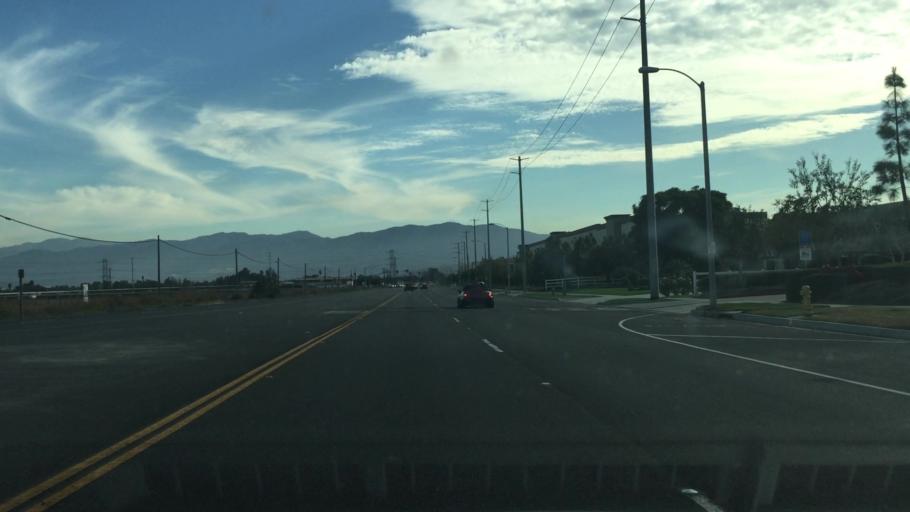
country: US
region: California
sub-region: San Bernardino County
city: Los Serranos
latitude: 33.9650
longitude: -117.6507
